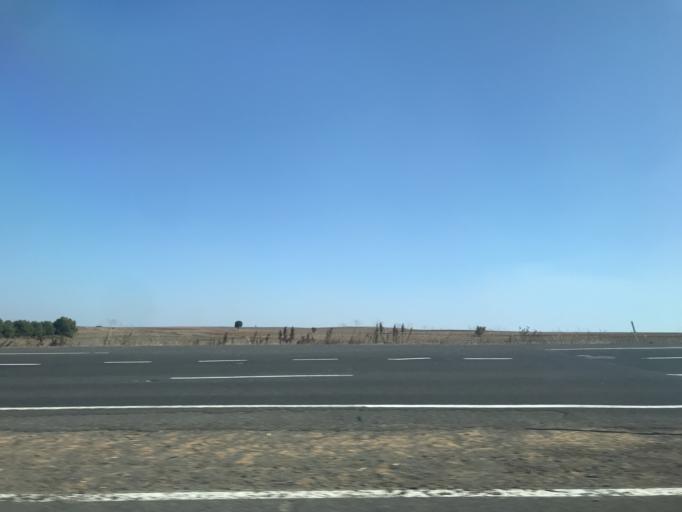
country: TR
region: Tekirdag
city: Muratli
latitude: 41.1414
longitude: 27.4939
